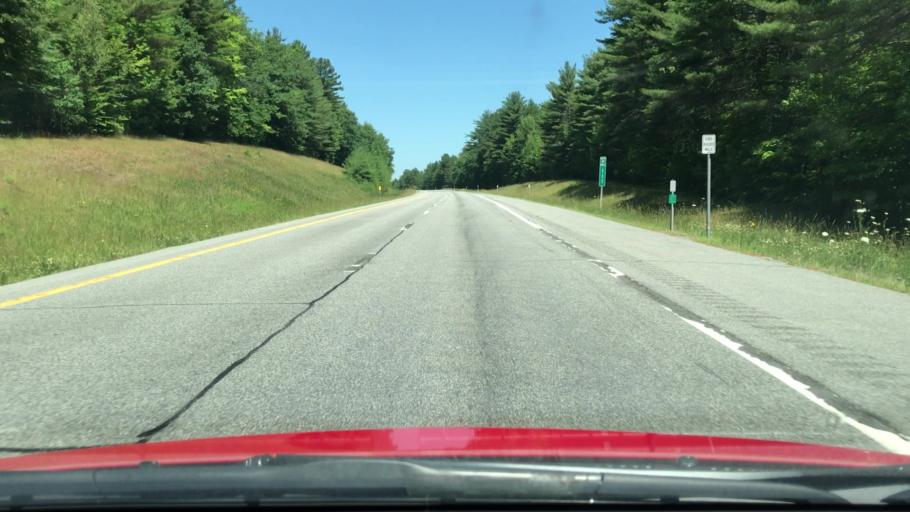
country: US
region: New York
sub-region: Essex County
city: Elizabethtown
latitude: 44.1499
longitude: -73.5829
